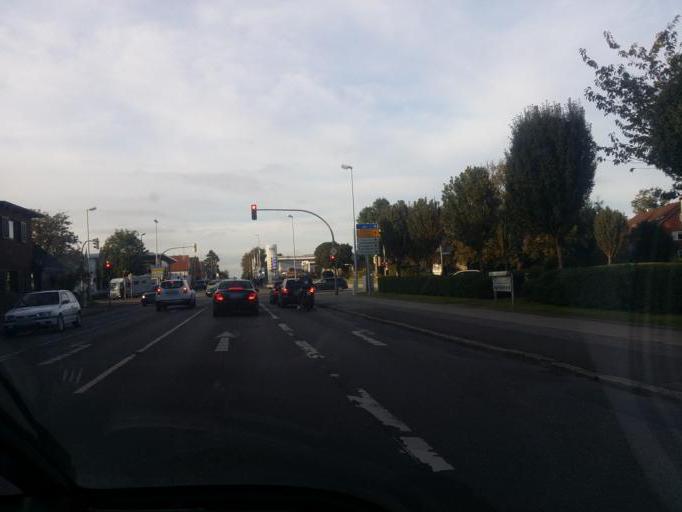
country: DE
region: Schleswig-Holstein
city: Husum
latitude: 54.4850
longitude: 9.0463
